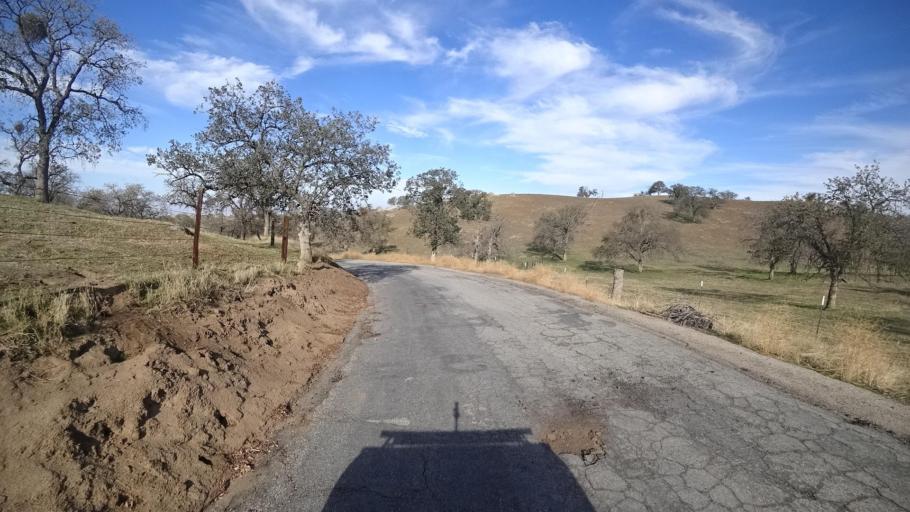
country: US
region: California
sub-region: Kern County
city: Oildale
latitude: 35.6100
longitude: -118.8357
